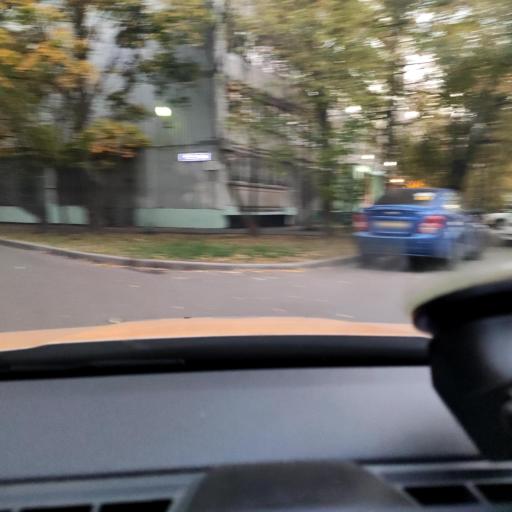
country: RU
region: Moscow
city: Babushkin
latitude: 55.8742
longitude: 37.7216
